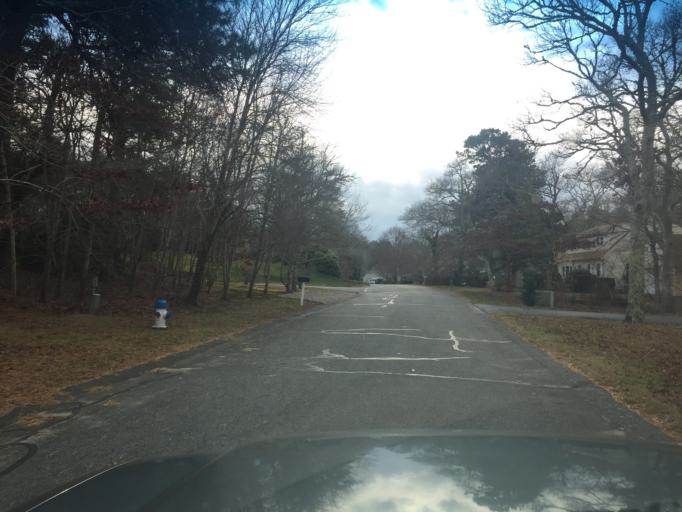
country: US
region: Massachusetts
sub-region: Barnstable County
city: North Falmouth
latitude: 41.6384
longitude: -70.6120
